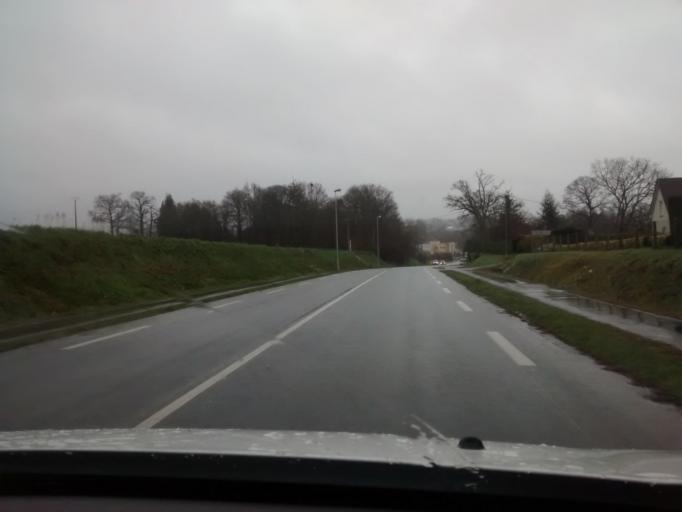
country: FR
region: Brittany
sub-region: Departement d'Ille-et-Vilaine
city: Acigne
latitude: 48.1376
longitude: -1.5533
